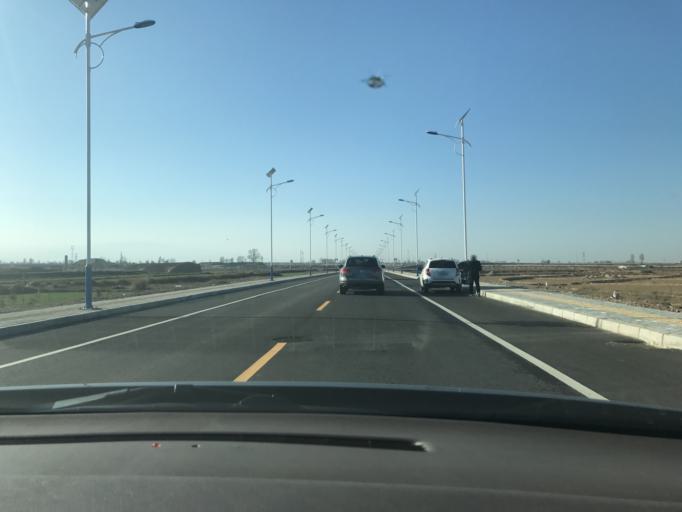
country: CN
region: Gansu Sheng
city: Gulang
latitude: 37.6256
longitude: 103.0007
